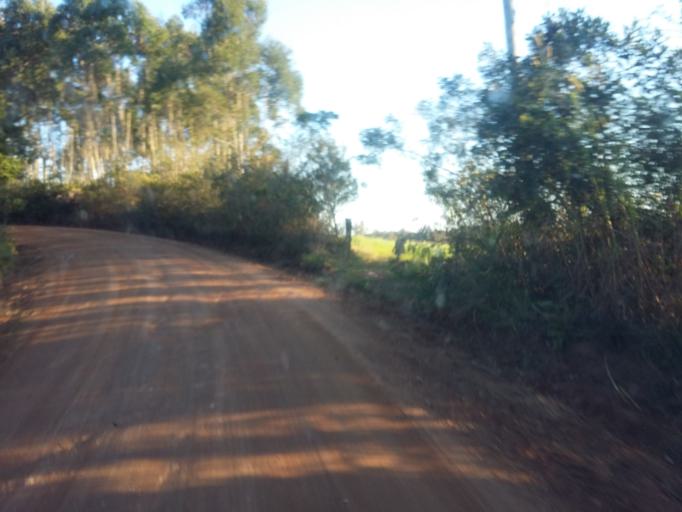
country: BR
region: Rio Grande do Sul
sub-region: Camaqua
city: Camaqua
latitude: -30.7064
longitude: -51.7681
